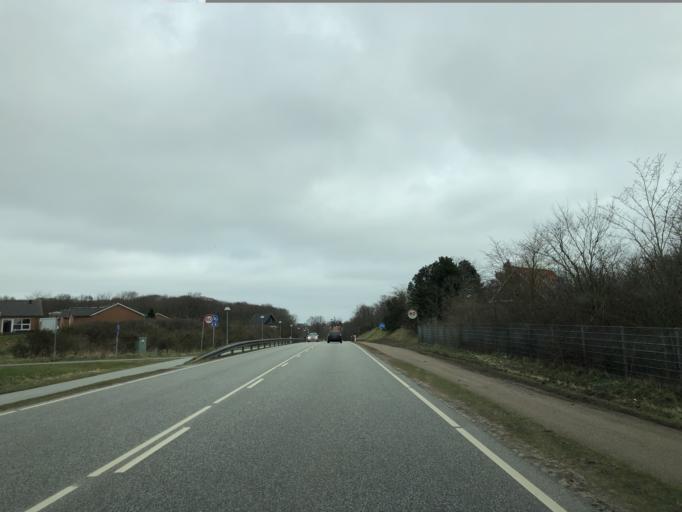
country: DK
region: North Denmark
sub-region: Frederikshavn Kommune
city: Saeby
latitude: 57.3332
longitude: 10.5082
